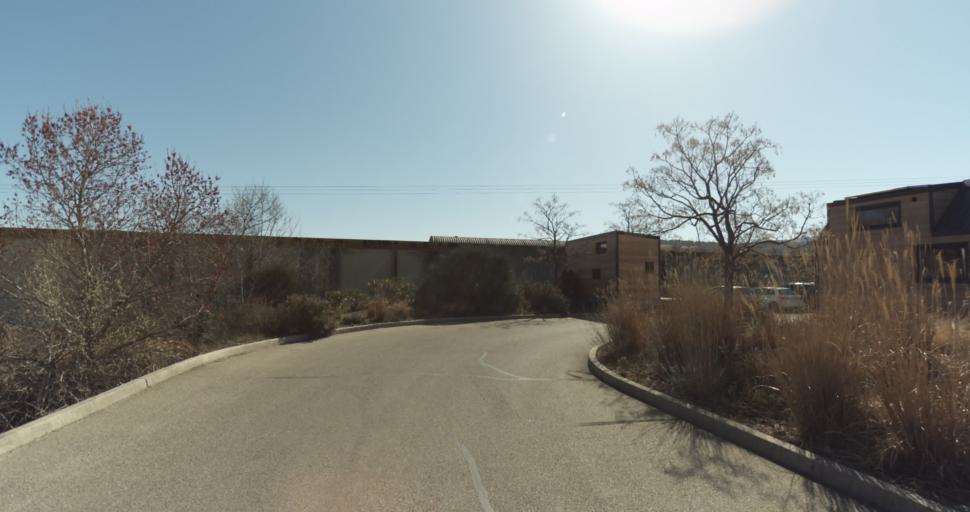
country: FR
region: Provence-Alpes-Cote d'Azur
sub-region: Departement des Bouches-du-Rhone
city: Charleval
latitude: 43.7233
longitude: 5.2822
